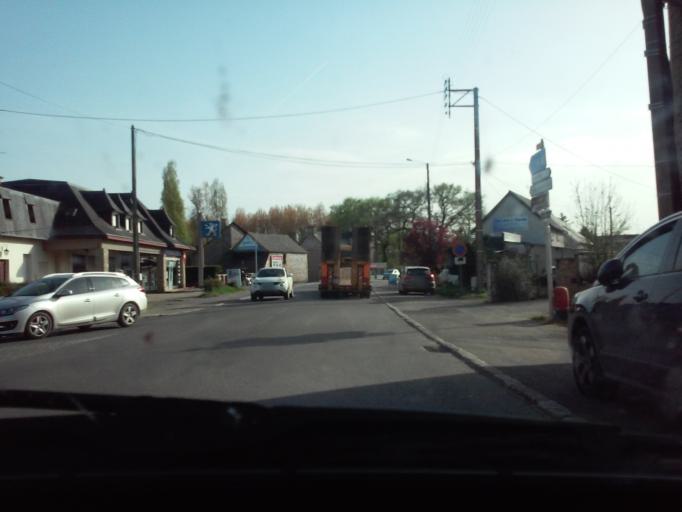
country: FR
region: Brittany
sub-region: Departement d'Ille-et-Vilaine
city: Saint-Aubin-du-Cormier
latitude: 48.2606
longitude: -1.4048
